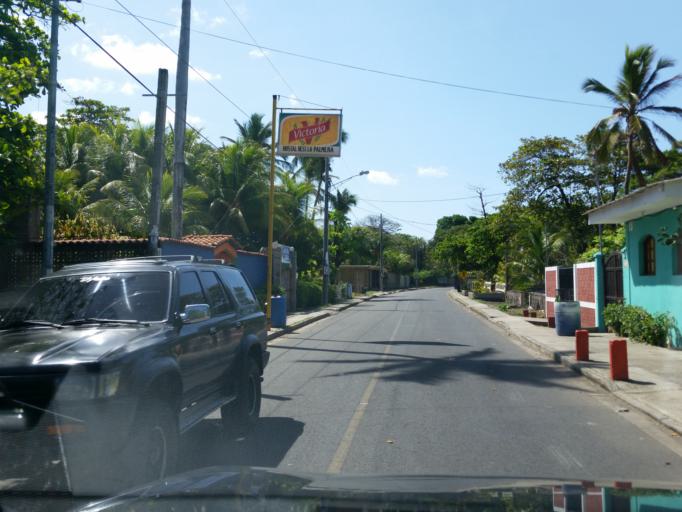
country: NI
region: Leon
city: Leon
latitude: 12.3629
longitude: -87.0256
